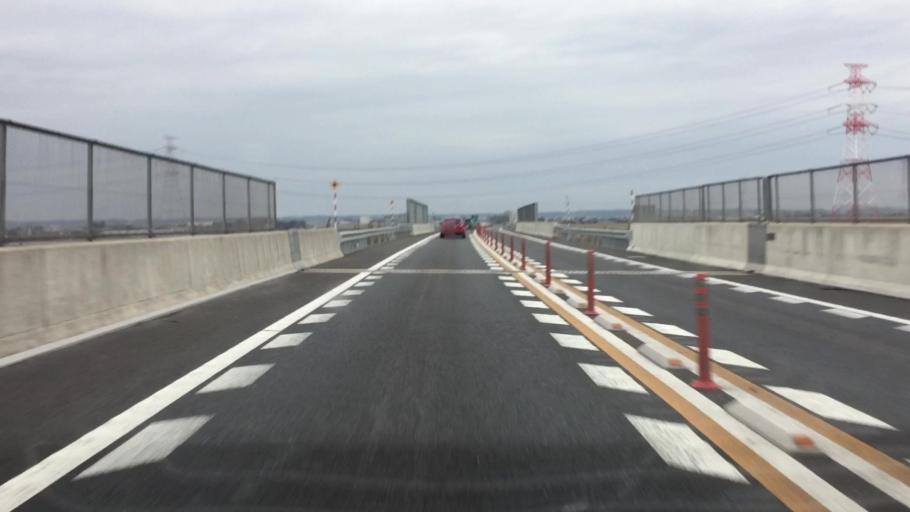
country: JP
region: Ibaraki
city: Inashiki
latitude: 35.8853
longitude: 140.3832
